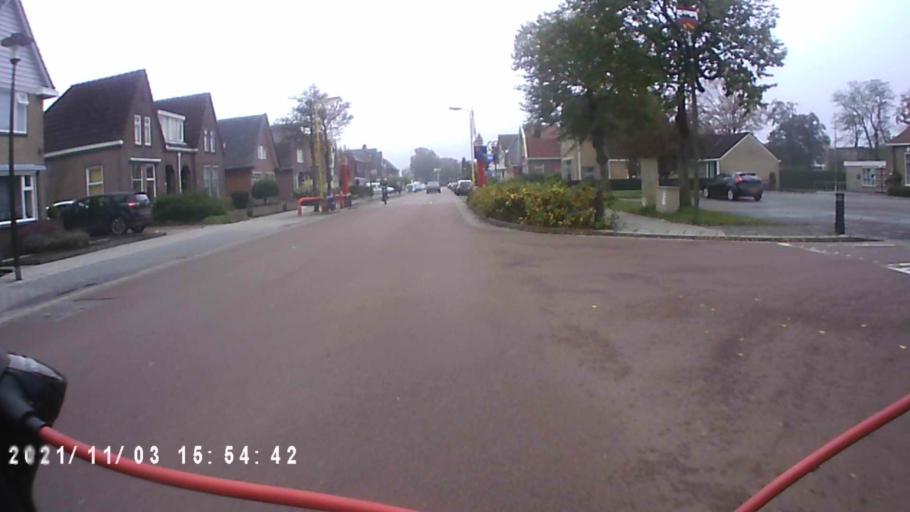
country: NL
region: Groningen
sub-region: Gemeente Leek
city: Leek
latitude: 53.0673
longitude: 6.3317
